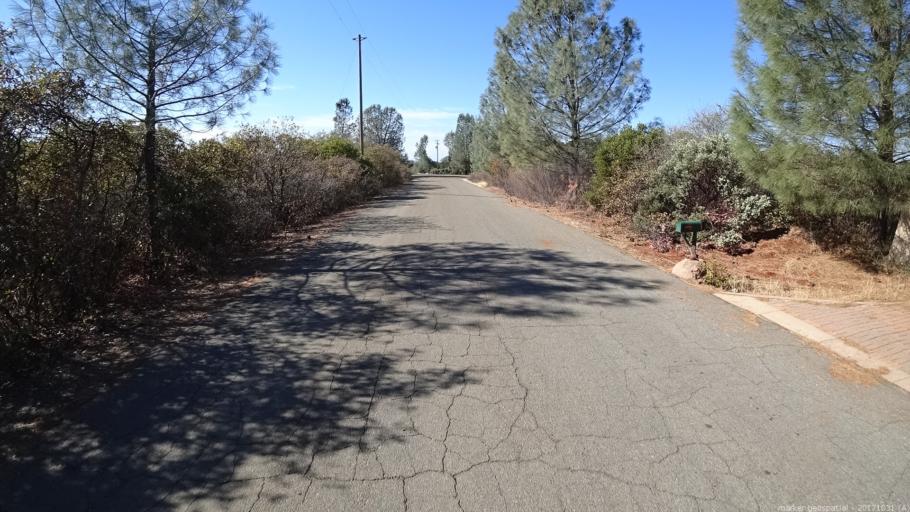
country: US
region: California
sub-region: Shasta County
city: Shingletown
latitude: 40.5088
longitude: -122.0276
